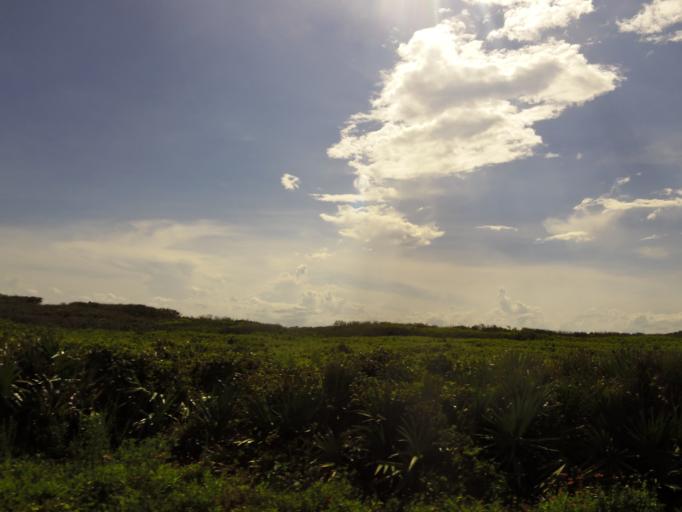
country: US
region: Florida
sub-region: Saint Johns County
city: Palm Valley
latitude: 30.0861
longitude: -81.3381
